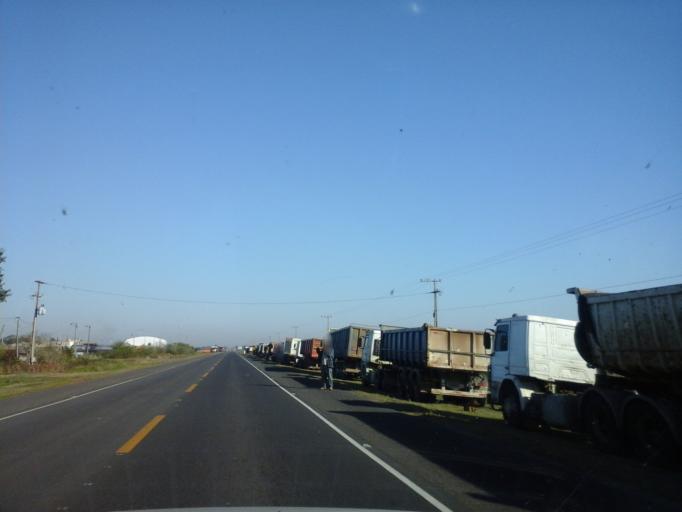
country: PY
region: Neembucu
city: Pilar
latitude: -26.8448
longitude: -58.2589
